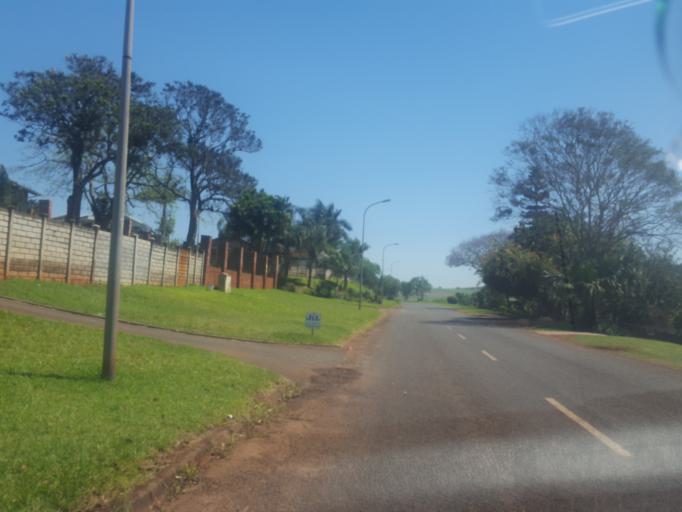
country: ZA
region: KwaZulu-Natal
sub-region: uThungulu District Municipality
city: Empangeni
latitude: -28.7461
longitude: 31.9086
